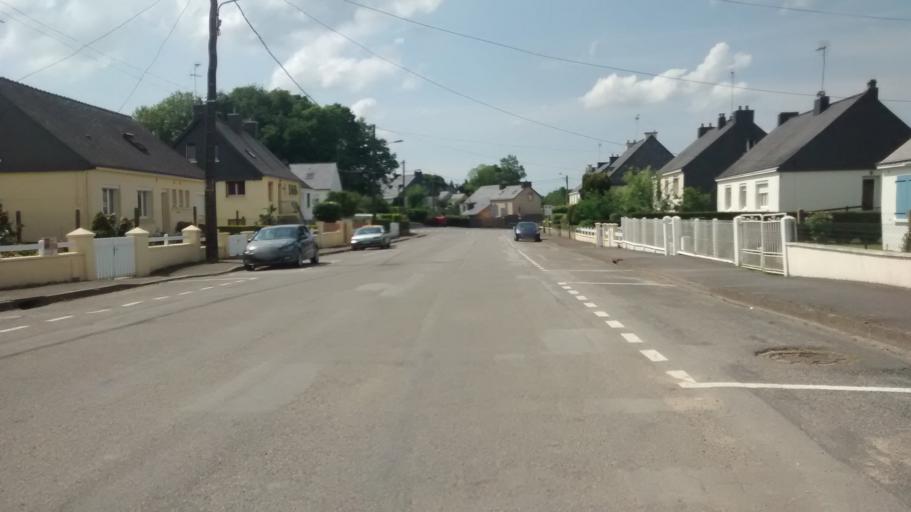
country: FR
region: Brittany
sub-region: Departement du Morbihan
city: Questembert
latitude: 47.6636
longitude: -2.4484
